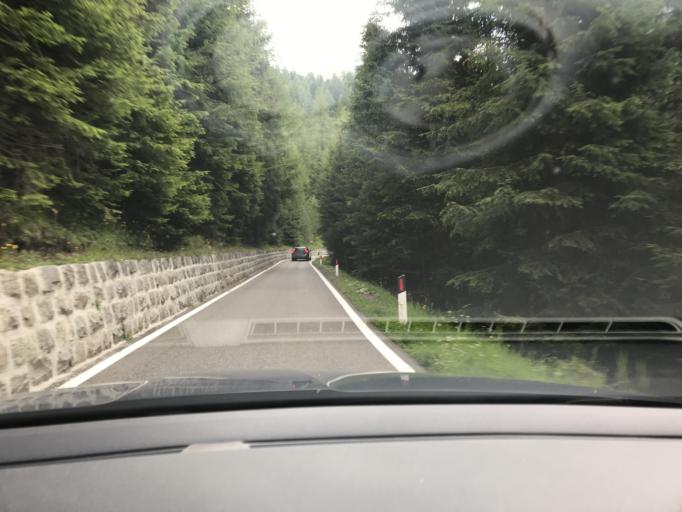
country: IT
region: Trentino-Alto Adige
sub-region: Bolzano
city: San Martino
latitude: 46.8907
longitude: 12.1912
